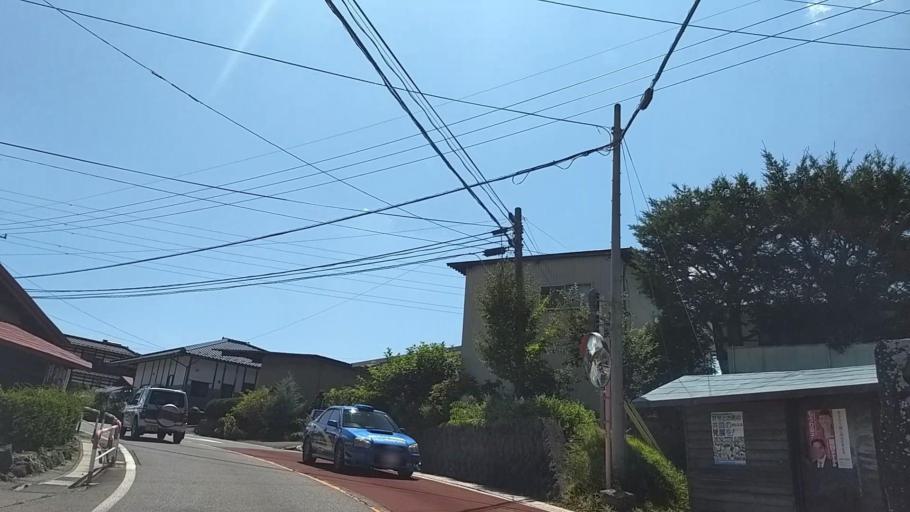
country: JP
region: Nagano
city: Chino
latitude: 36.0376
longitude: 138.2238
